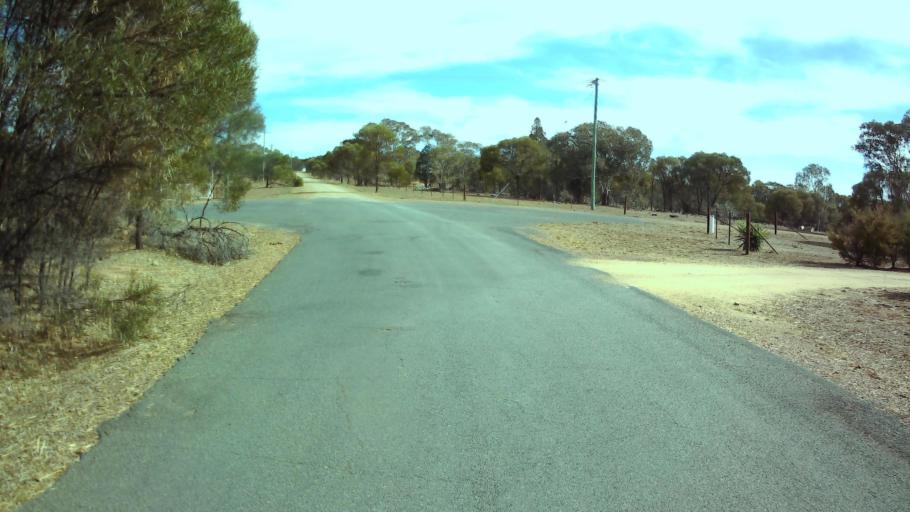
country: AU
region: New South Wales
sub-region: Weddin
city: Grenfell
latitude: -33.8759
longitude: 148.1926
